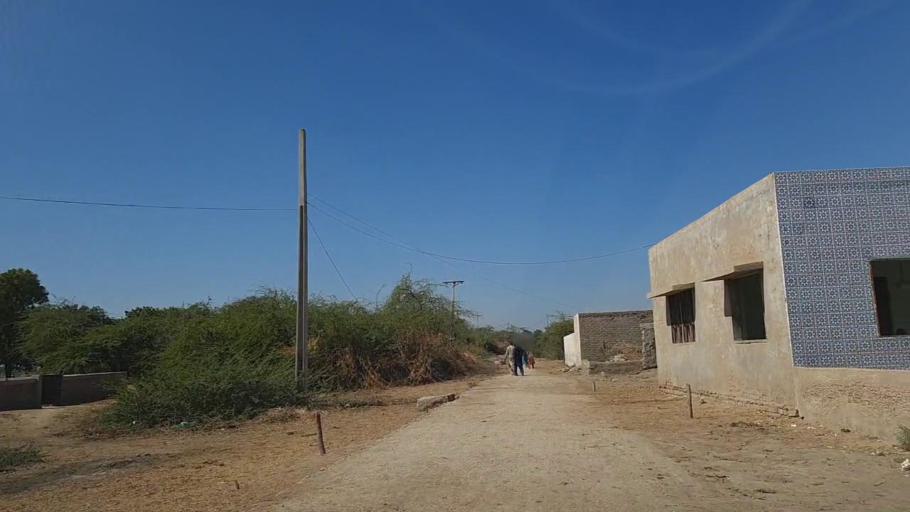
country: PK
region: Sindh
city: Samaro
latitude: 25.3433
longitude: 69.4863
